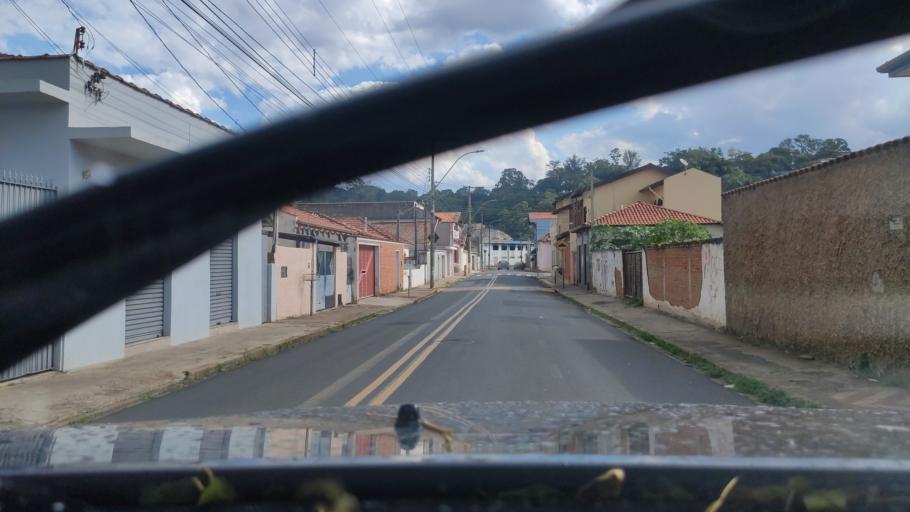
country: BR
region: Sao Paulo
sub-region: Itapira
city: Itapira
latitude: -22.4378
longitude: -46.8168
